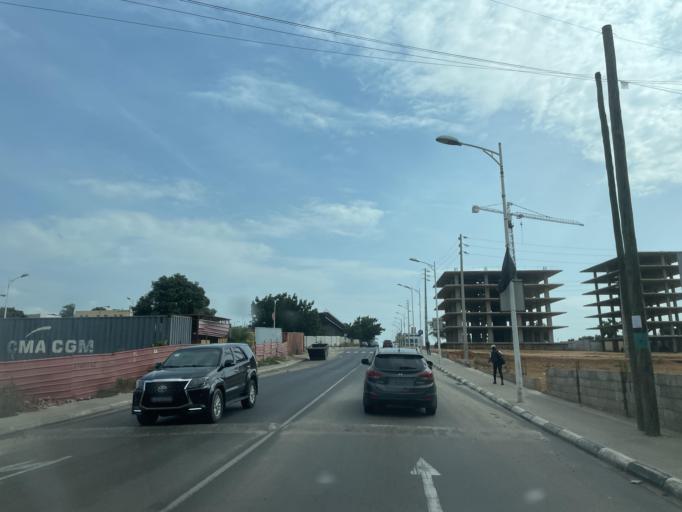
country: AO
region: Luanda
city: Luanda
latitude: -8.9451
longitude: 13.1893
